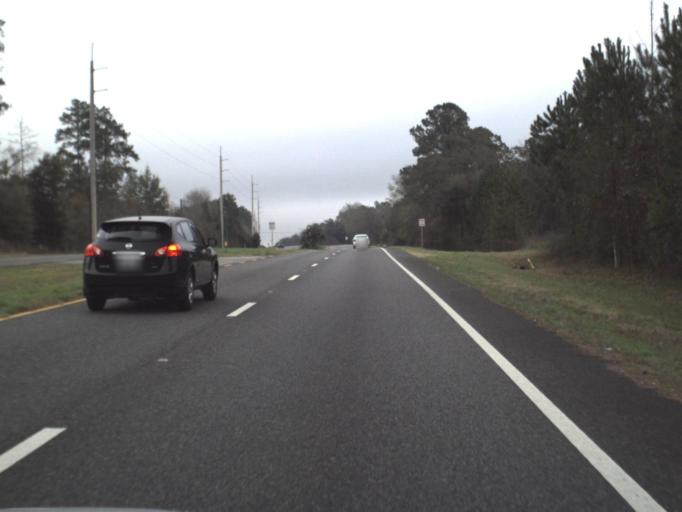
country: US
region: Florida
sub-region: Jefferson County
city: Monticello
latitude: 30.4092
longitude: -83.9683
